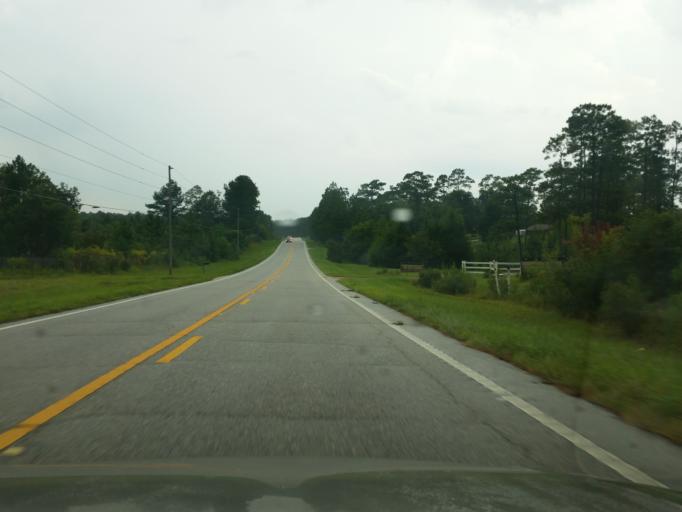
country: US
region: Alabama
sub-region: Baldwin County
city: Elberta
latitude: 30.5224
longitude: -87.4919
